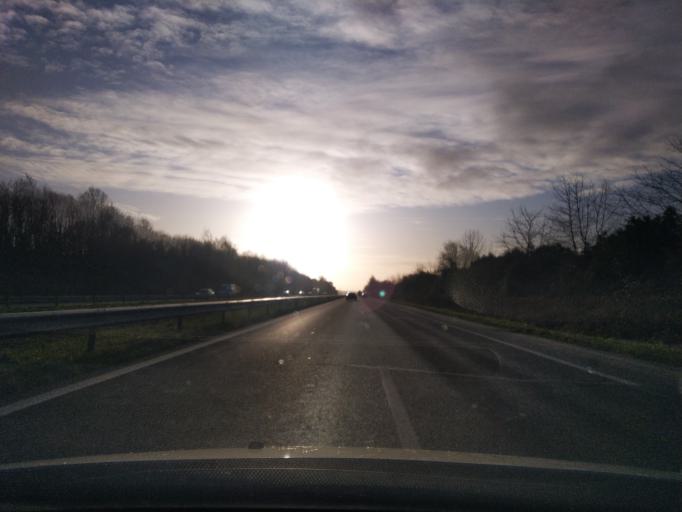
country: FR
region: Haute-Normandie
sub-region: Departement de la Seine-Maritime
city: Maromme
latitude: 49.4777
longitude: 1.0173
